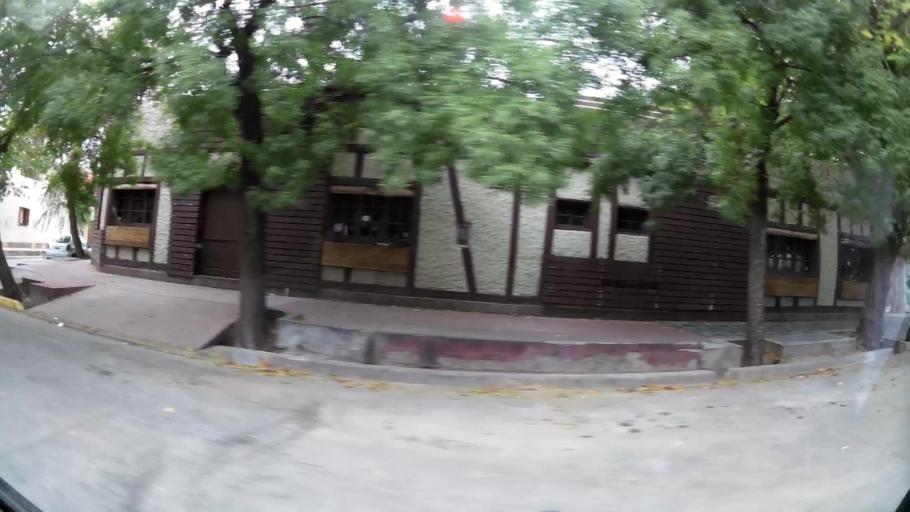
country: AR
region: Mendoza
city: Mendoza
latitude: -32.8915
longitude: -68.8581
